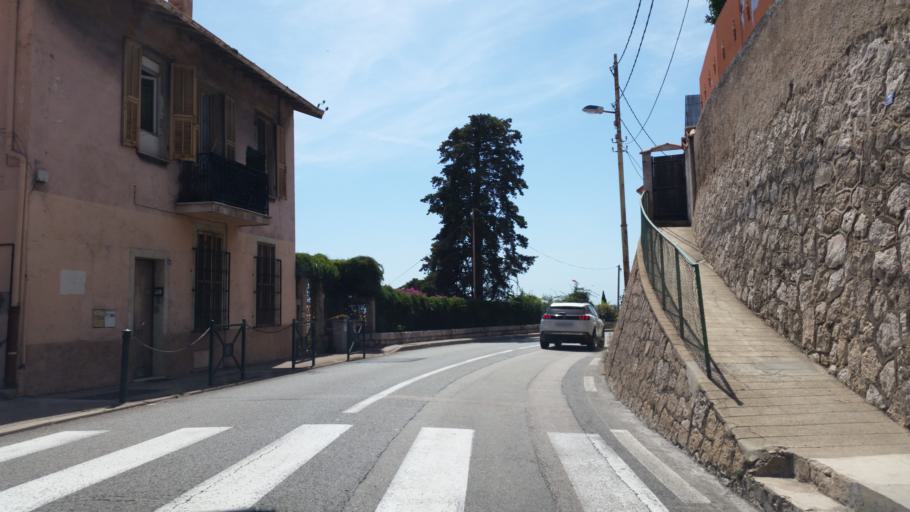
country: MC
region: Commune de Monaco
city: Saint-Roman
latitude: 43.7615
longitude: 7.4541
